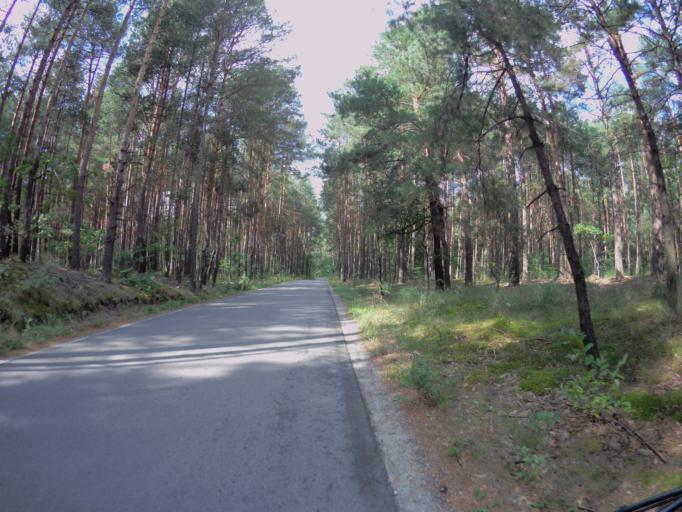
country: PL
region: Subcarpathian Voivodeship
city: Nowa Sarzyna
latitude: 50.3057
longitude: 22.3462
